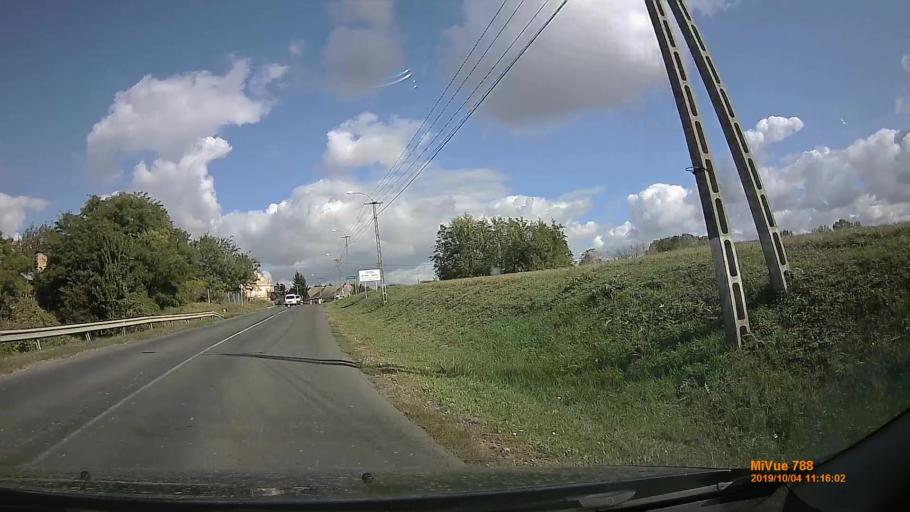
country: HU
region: Somogy
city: Kaposvar
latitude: 46.4524
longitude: 17.8046
